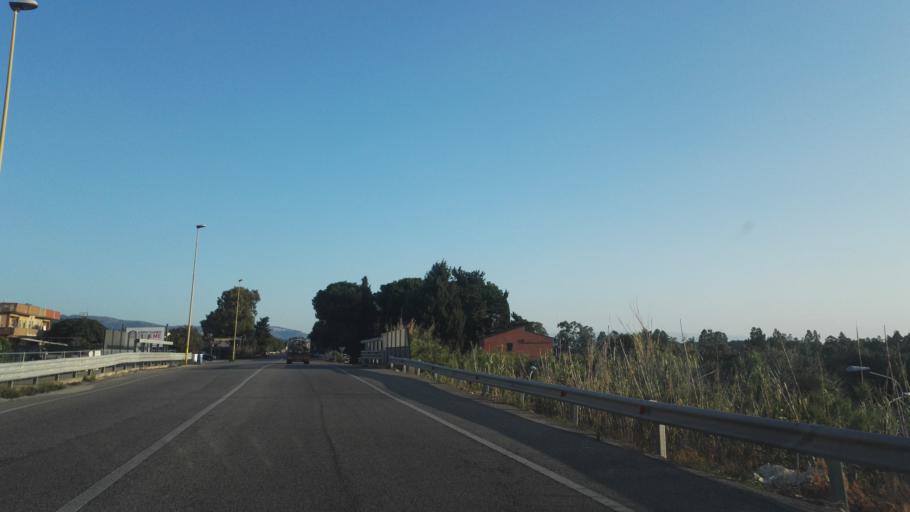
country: IT
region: Calabria
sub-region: Provincia di Catanzaro
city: Isca Marina
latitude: 38.6055
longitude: 16.5566
